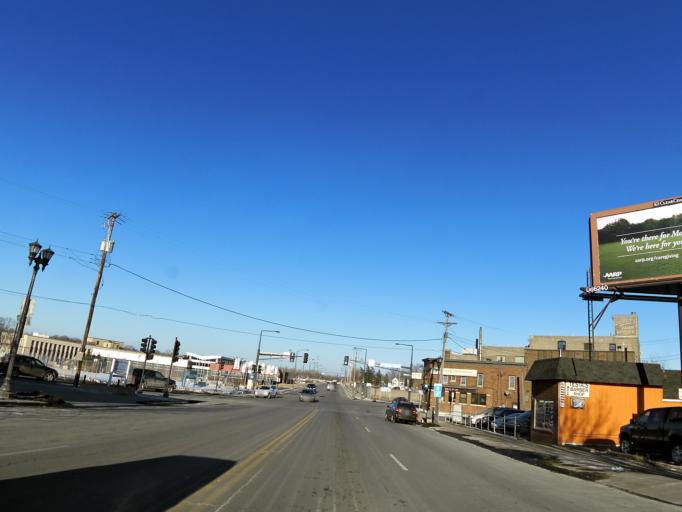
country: US
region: Minnesota
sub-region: Ramsey County
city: Saint Paul
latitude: 44.9626
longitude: -93.0643
